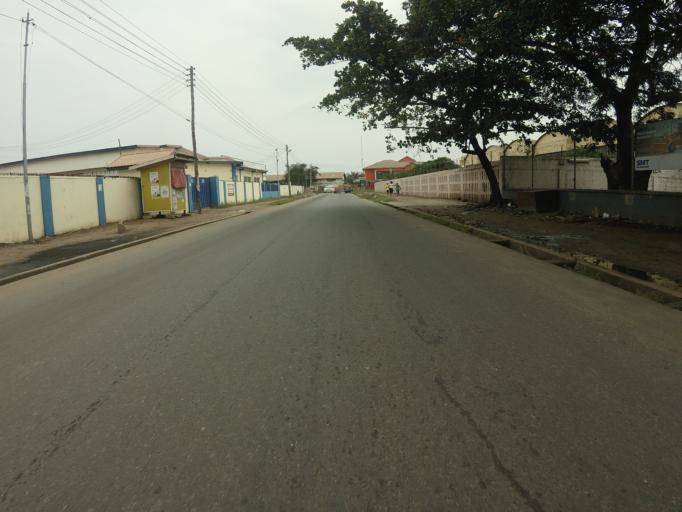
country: GH
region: Greater Accra
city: Accra
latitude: 5.5559
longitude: -0.2233
